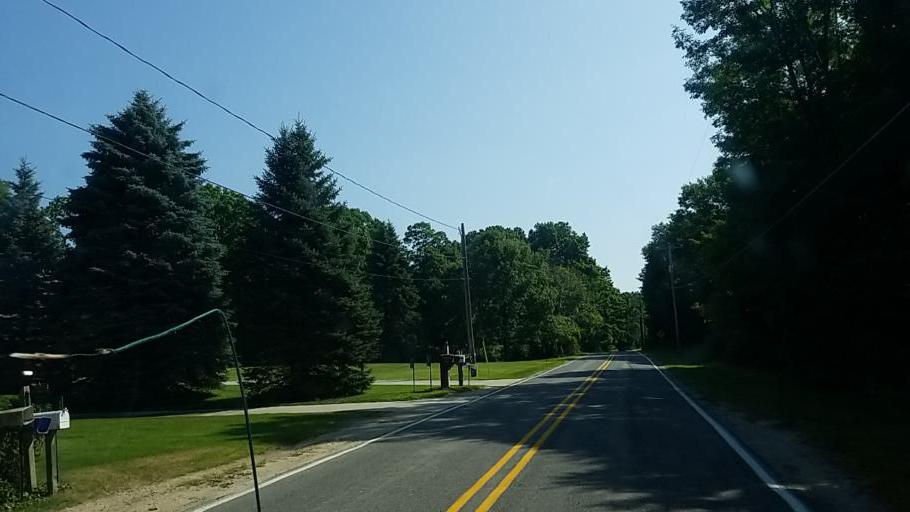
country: US
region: Michigan
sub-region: Muskegon County
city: Whitehall
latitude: 43.3681
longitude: -86.3884
